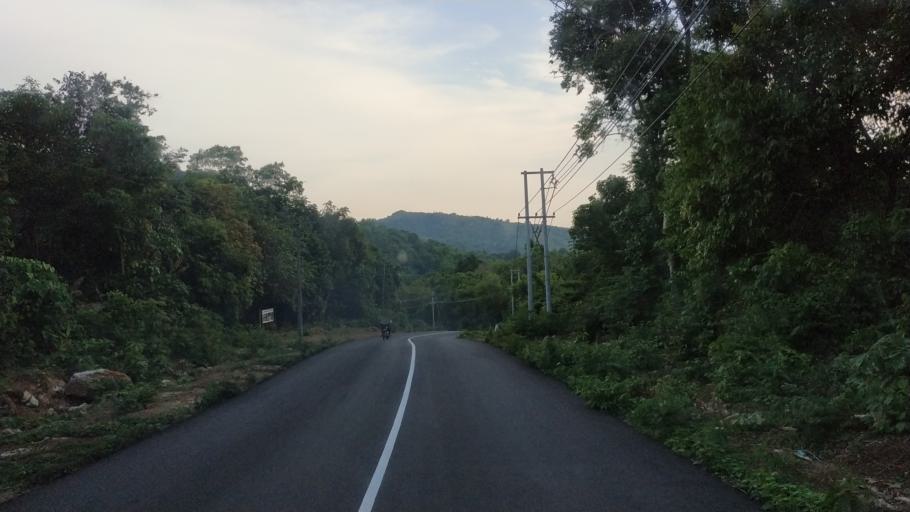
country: MM
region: Mon
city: Kyaikto
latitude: 17.4343
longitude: 97.0947
